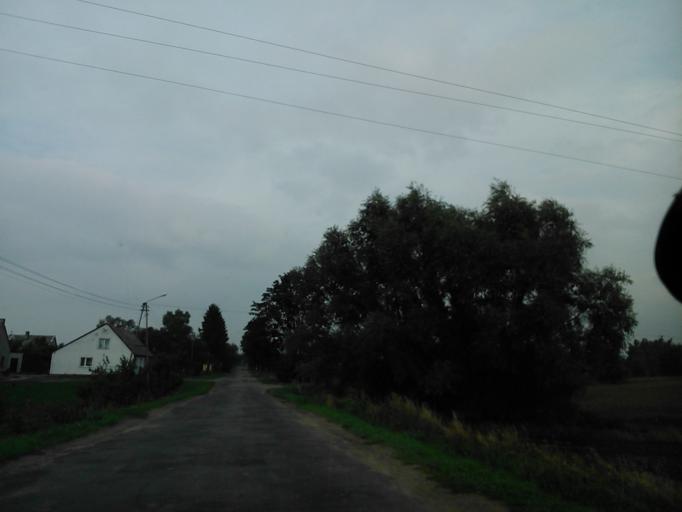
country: PL
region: Kujawsko-Pomorskie
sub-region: Powiat wabrzeski
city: Pluznica
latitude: 53.2523
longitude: 18.8264
